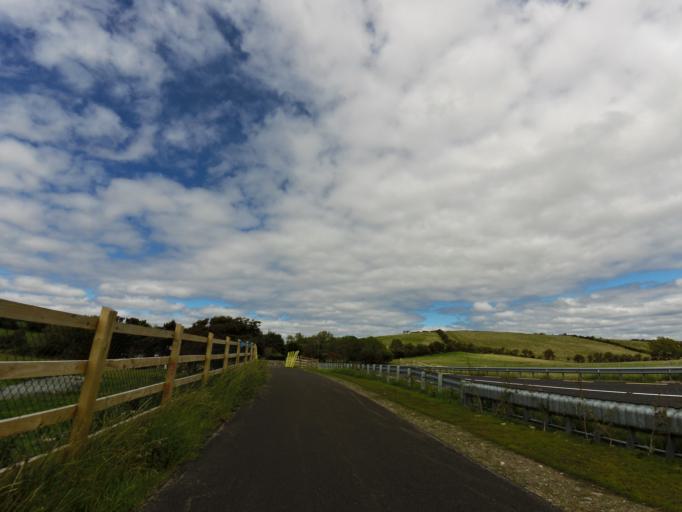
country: IE
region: Connaught
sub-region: Maigh Eo
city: Westport
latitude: 53.8388
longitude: -9.5526
